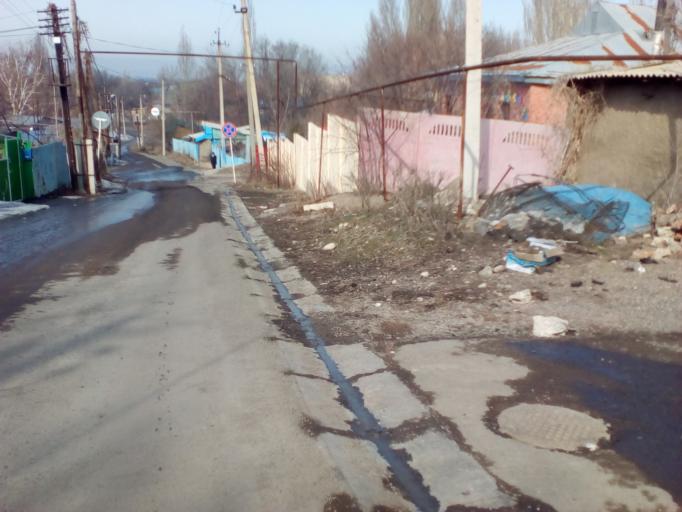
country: KZ
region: Almaty Oblysy
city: Burunday
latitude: 43.1531
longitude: 76.4175
